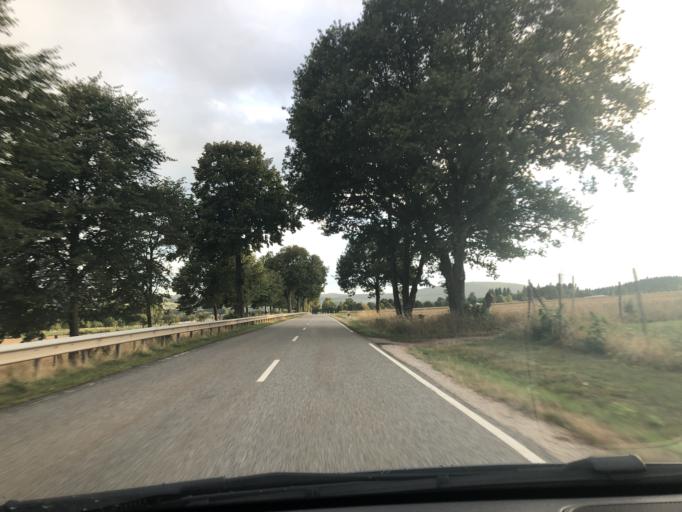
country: DE
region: Rheinland-Pfalz
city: Gusenburg
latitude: 49.6443
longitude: 6.9061
